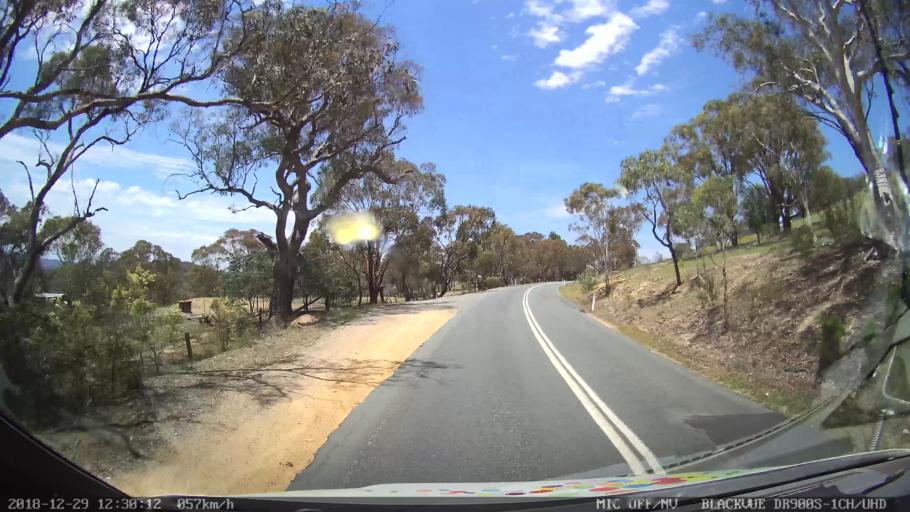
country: AU
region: Australian Capital Territory
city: Macarthur
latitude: -35.5040
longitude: 149.2332
